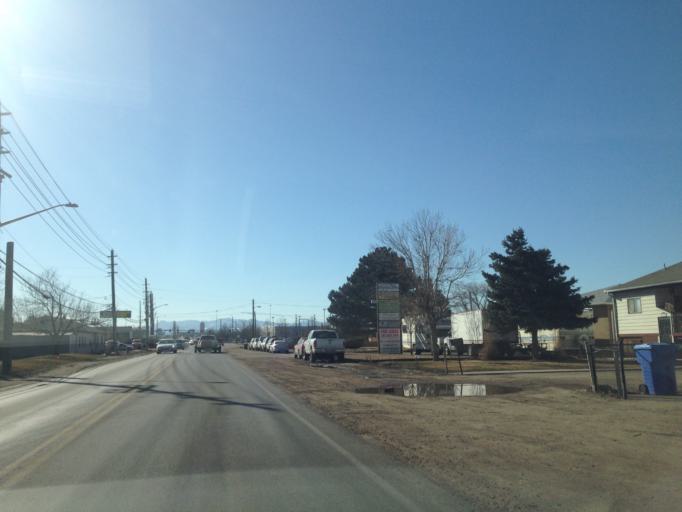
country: US
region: Colorado
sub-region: Adams County
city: Welby
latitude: 39.8019
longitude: -104.9743
